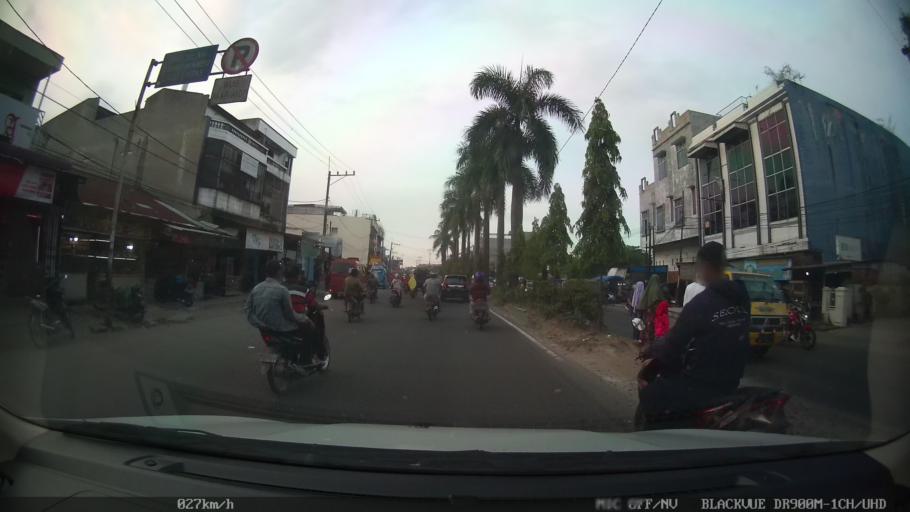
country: ID
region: North Sumatra
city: Sunggal
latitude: 3.5958
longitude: 98.6092
